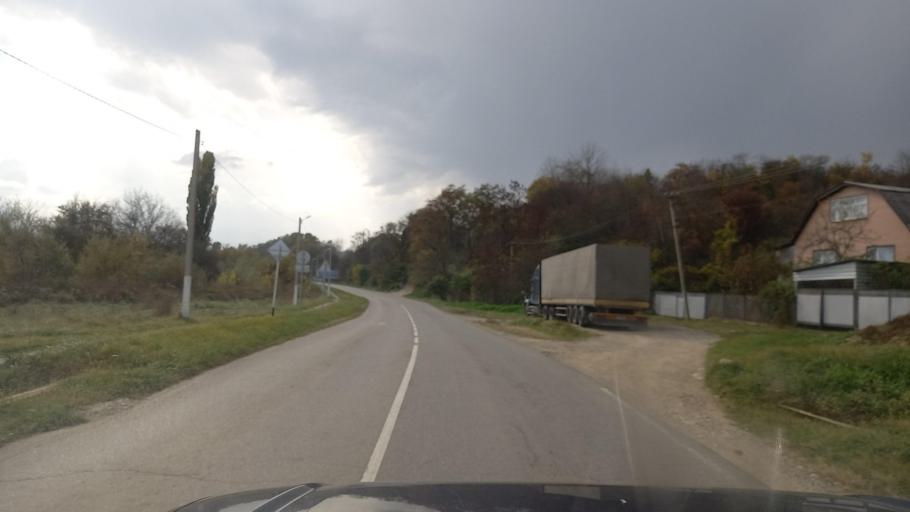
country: RU
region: Krasnodarskiy
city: Psebay
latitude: 44.1313
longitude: 40.8112
